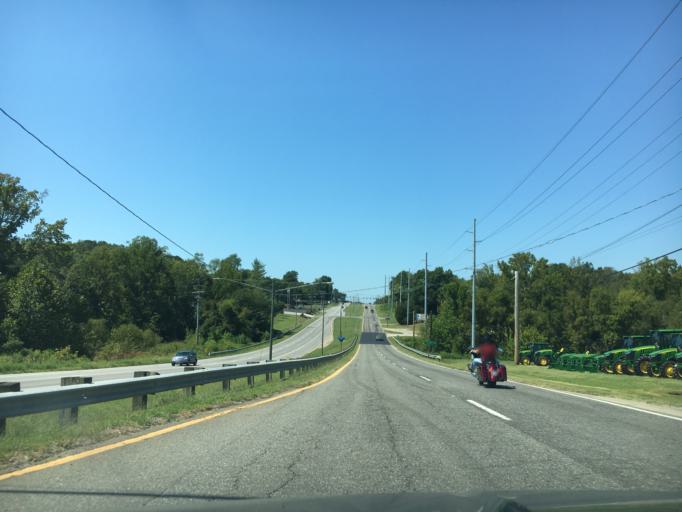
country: US
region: Virginia
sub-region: City of Danville
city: Danville
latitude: 36.5810
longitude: -79.3148
